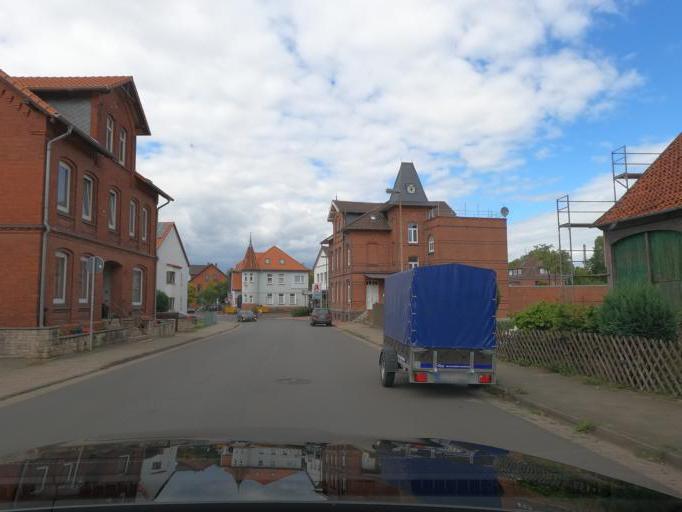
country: DE
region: Lower Saxony
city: Algermissen
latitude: 52.2532
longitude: 9.9655
